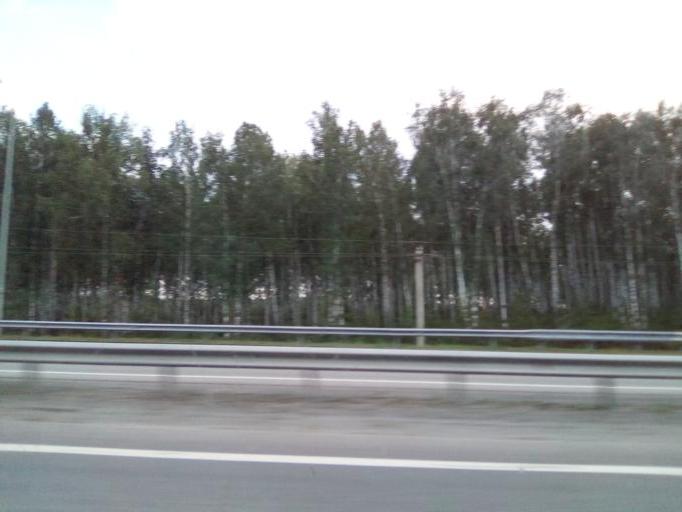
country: RU
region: Chelyabinsk
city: Poletayevo
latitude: 54.9945
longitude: 61.1246
